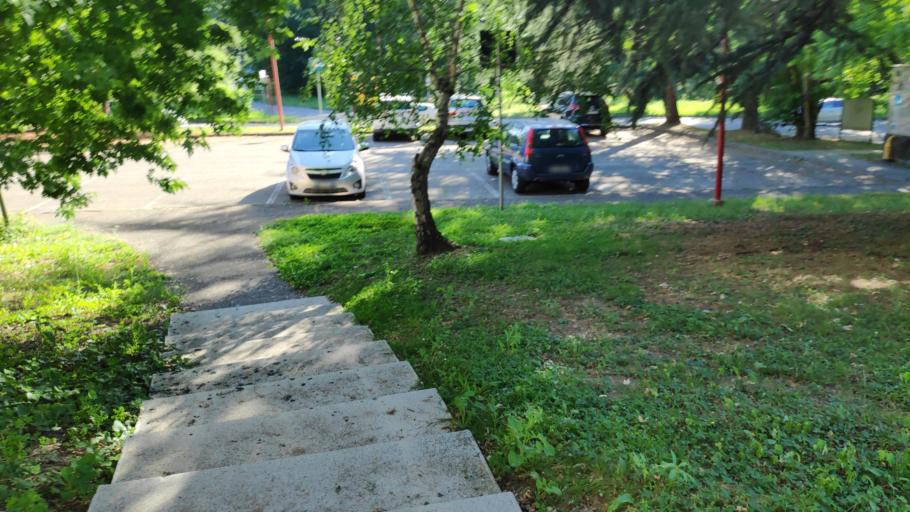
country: IT
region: Lombardy
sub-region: Citta metropolitana di Milano
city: Basiglio
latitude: 45.3568
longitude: 9.1485
